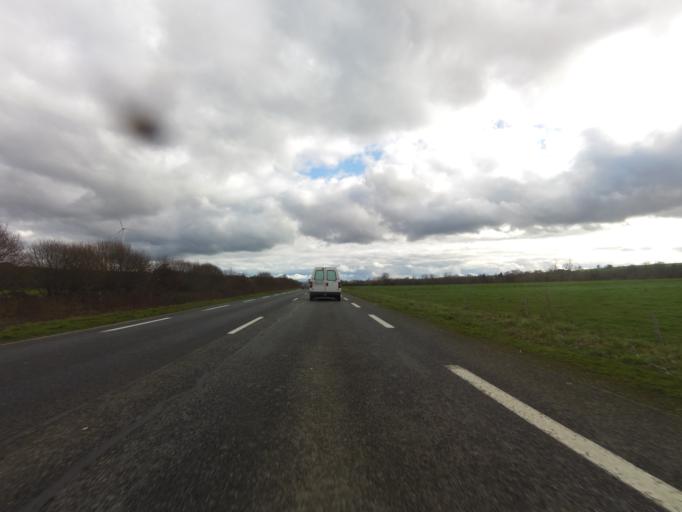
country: FR
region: Brittany
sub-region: Departement du Morbihan
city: Lanouee
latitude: 47.9640
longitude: -2.6123
